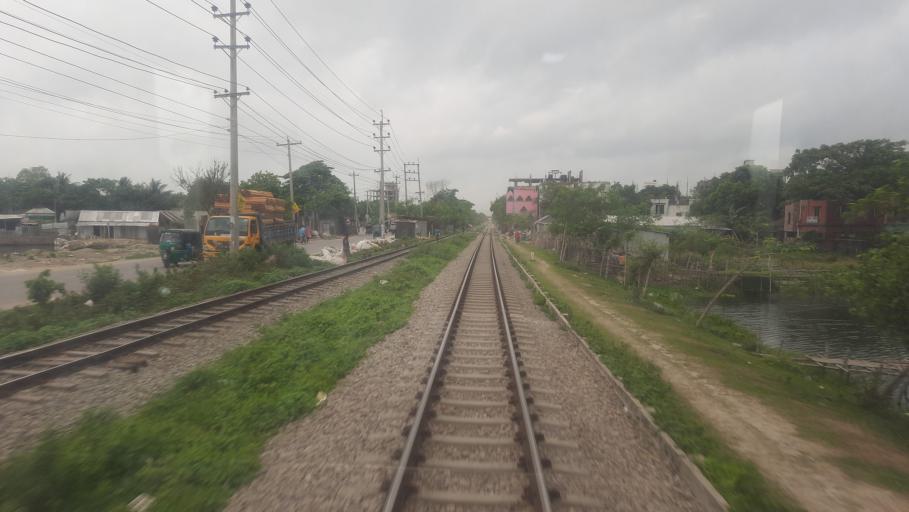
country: BD
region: Dhaka
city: Narsingdi
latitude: 23.9310
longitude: 90.7149
